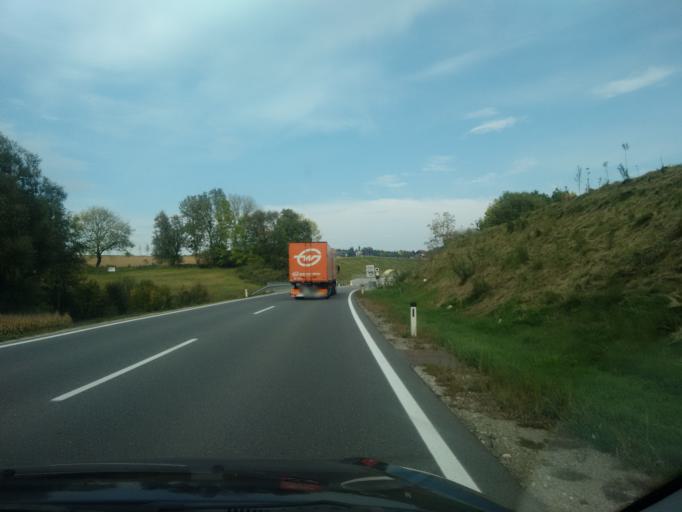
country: AT
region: Upper Austria
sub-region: Wels-Land
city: Stadl-Paura
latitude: 48.0971
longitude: 13.8547
